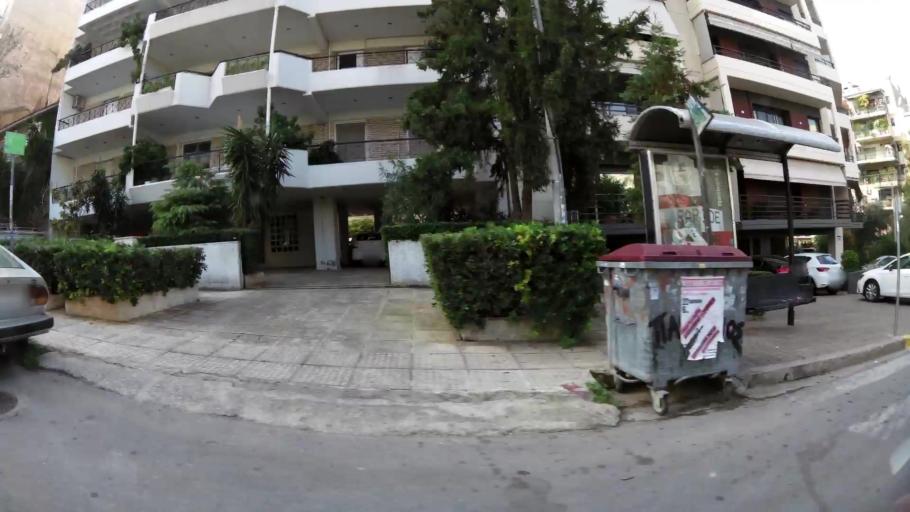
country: GR
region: Attica
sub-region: Nomarchia Athinas
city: Nea Smyrni
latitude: 37.9426
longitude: 23.7056
